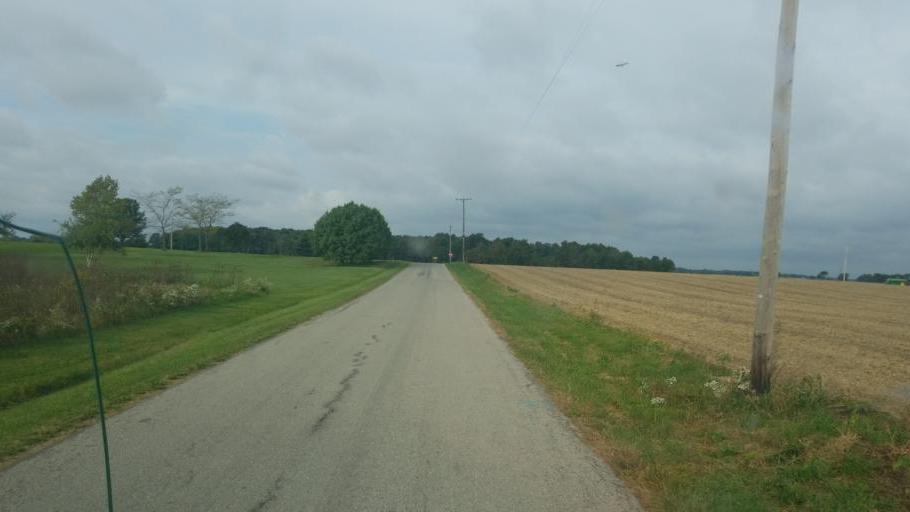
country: US
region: Ohio
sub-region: Seneca County
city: Fostoria
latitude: 41.0502
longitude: -83.4942
